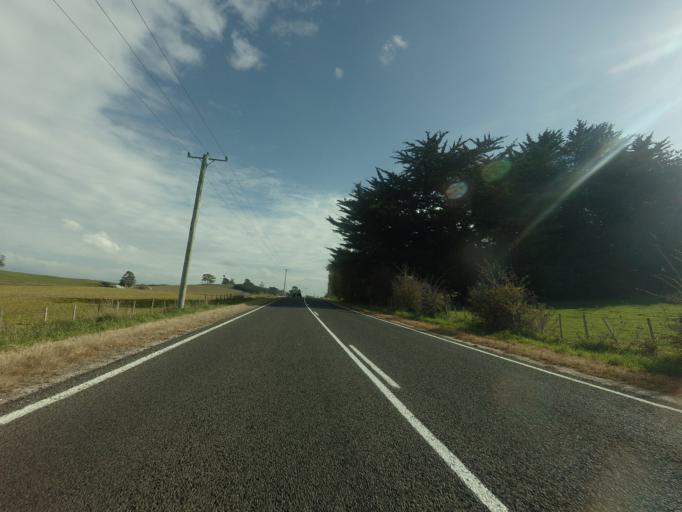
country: AU
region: Tasmania
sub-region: Meander Valley
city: Deloraine
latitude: -41.5255
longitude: 146.6976
